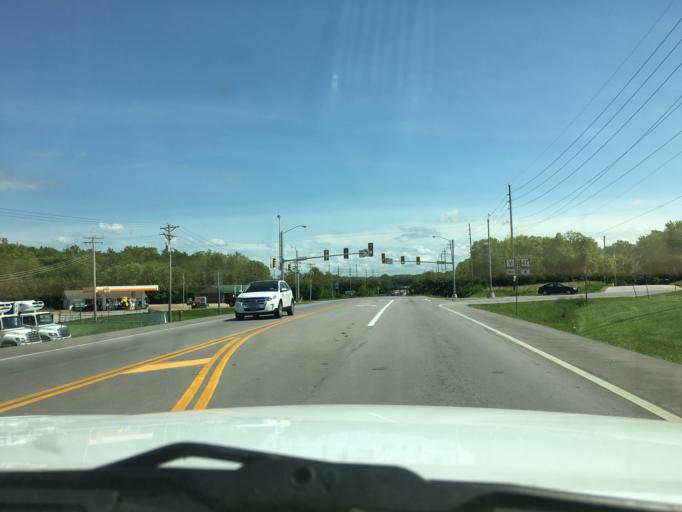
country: US
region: Missouri
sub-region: Franklin County
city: Union
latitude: 38.4554
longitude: -91.0026
